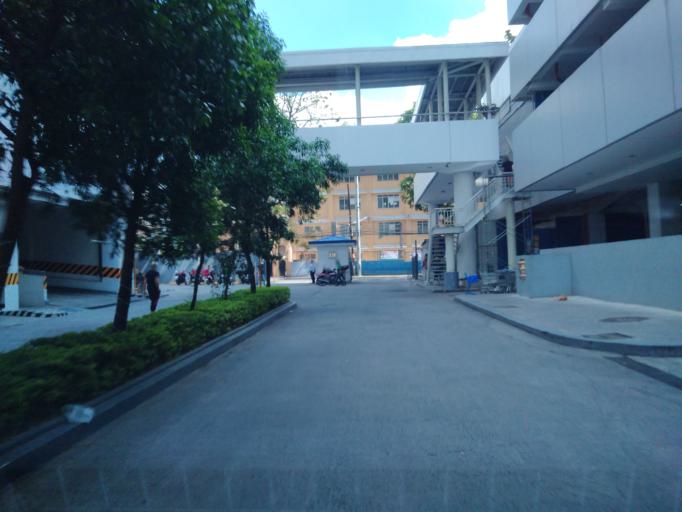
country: PH
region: Calabarzon
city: Bagong Pagasa
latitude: 14.6591
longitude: 121.0287
